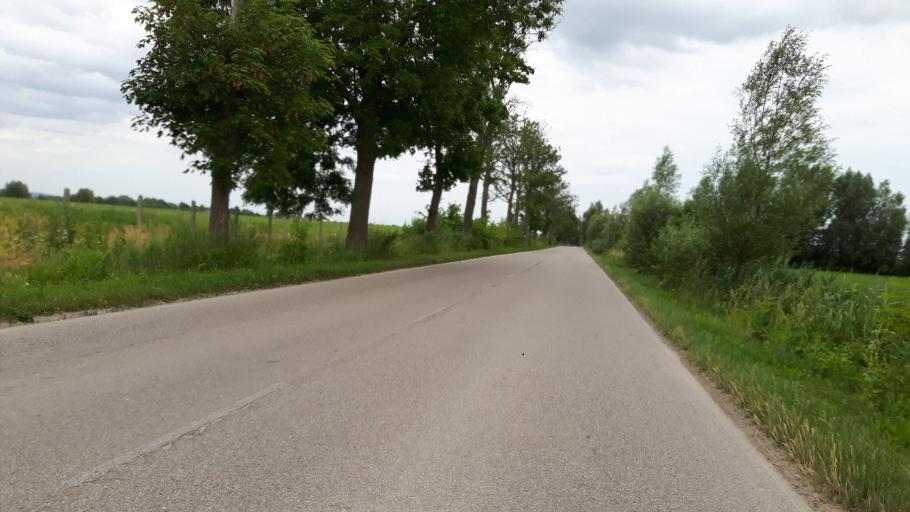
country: PL
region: Warmian-Masurian Voivodeship
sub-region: Powiat elblaski
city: Gronowo Elblaskie
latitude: 54.1964
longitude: 19.2915
